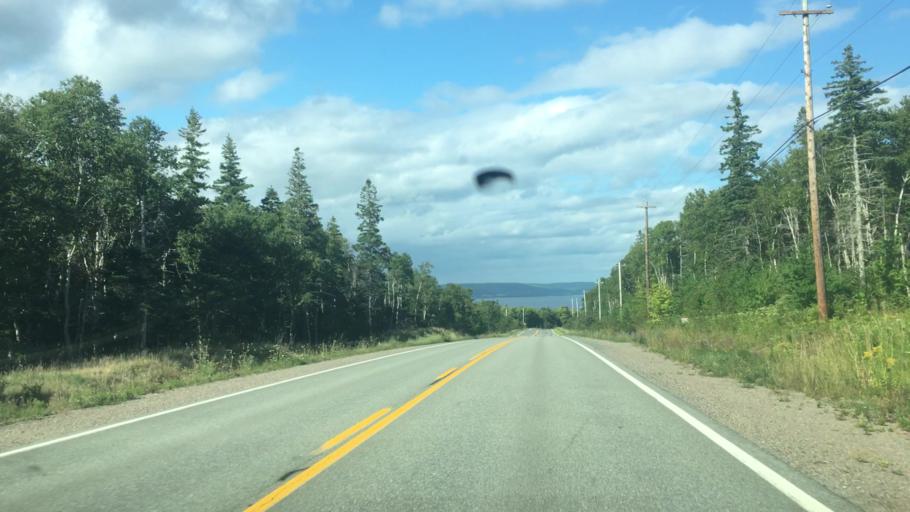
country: CA
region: Nova Scotia
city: Sydney
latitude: 45.8604
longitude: -60.6270
